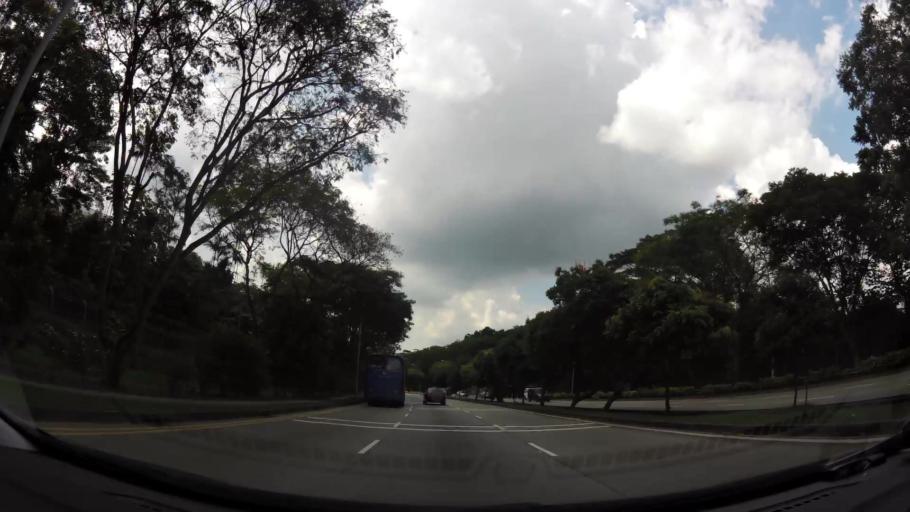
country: MY
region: Johor
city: Johor Bahru
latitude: 1.4153
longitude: 103.8102
